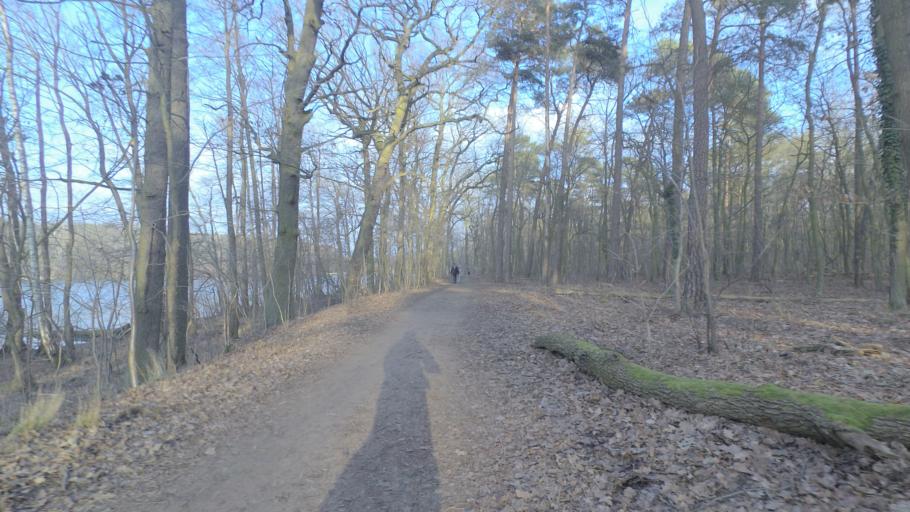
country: DE
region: Brandenburg
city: Rangsdorf
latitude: 52.3003
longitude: 13.4134
